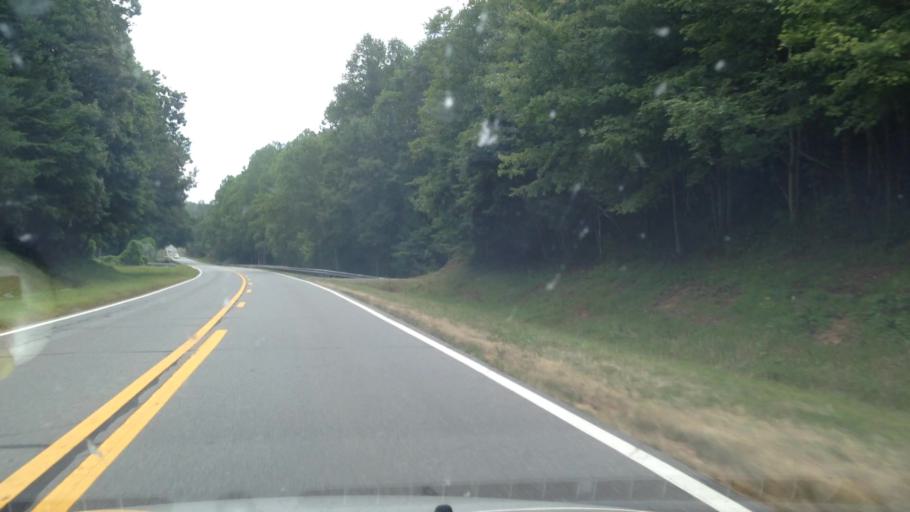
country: US
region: North Carolina
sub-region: Rockingham County
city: Madison
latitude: 36.3791
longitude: -79.8828
